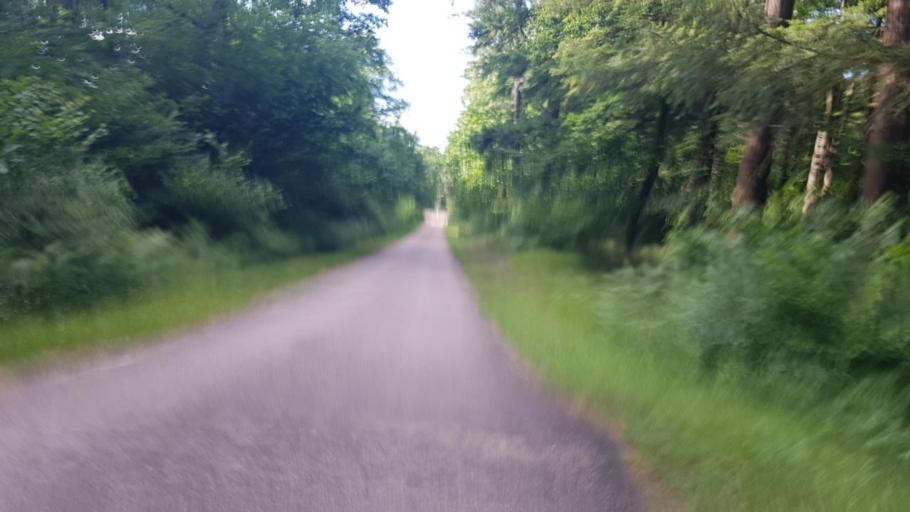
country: FR
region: Picardie
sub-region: Departement de l'Oise
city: Chamant
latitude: 49.1688
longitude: 2.6325
